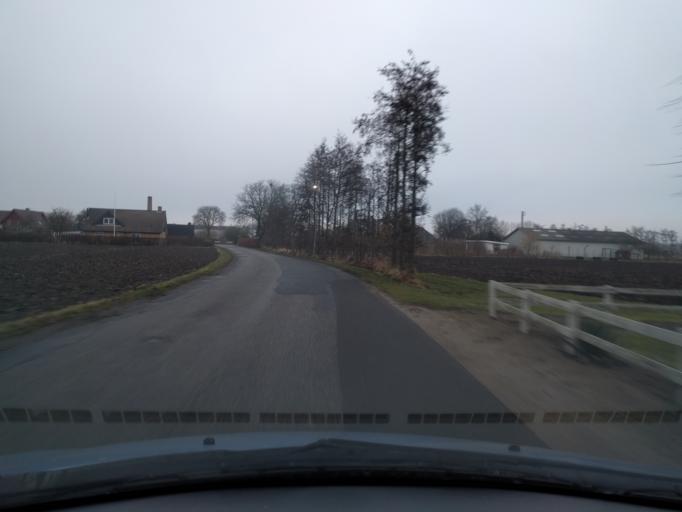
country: DK
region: South Denmark
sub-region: Odense Kommune
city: Bullerup
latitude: 55.4072
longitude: 10.5113
